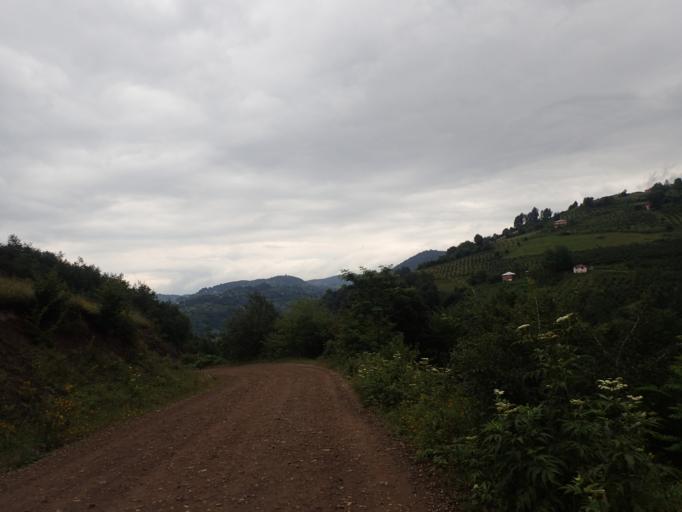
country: TR
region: Ordu
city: Akkus
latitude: 40.8144
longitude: 37.0980
